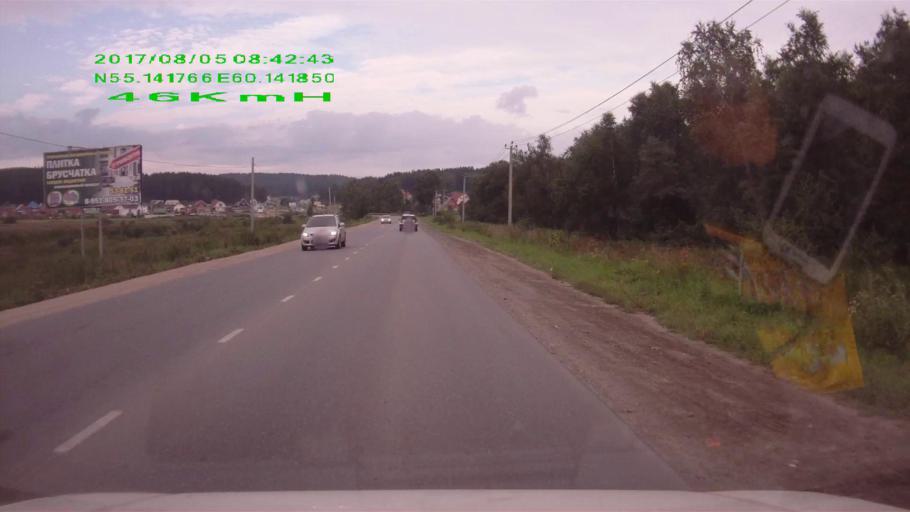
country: RU
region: Chelyabinsk
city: Turgoyak
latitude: 55.1418
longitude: 60.1418
